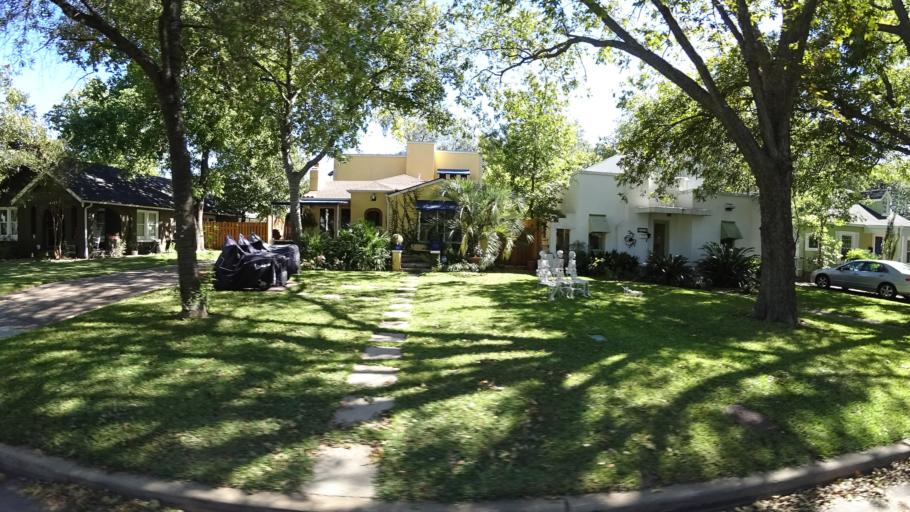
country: US
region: Texas
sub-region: Travis County
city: Austin
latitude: 30.3163
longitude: -97.7444
